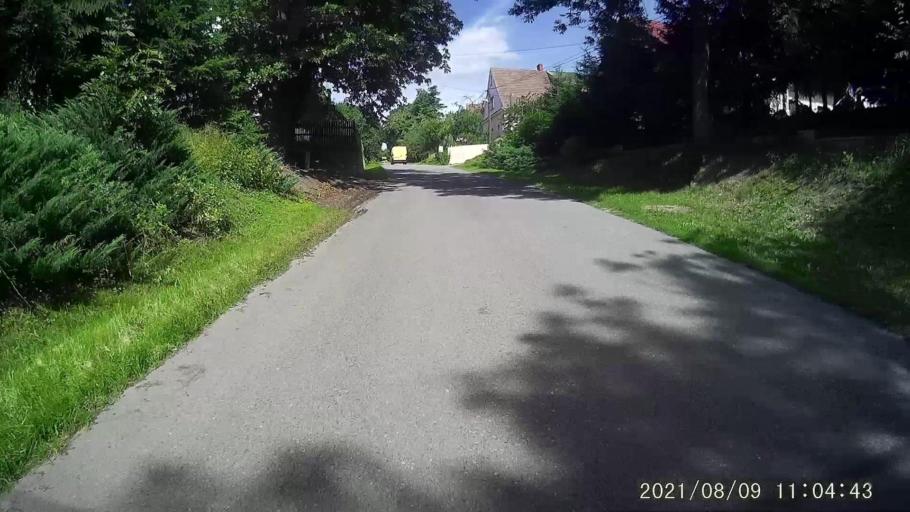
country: PL
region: Lower Silesian Voivodeship
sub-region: Powiat klodzki
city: Bozkow
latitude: 50.4629
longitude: 16.5738
